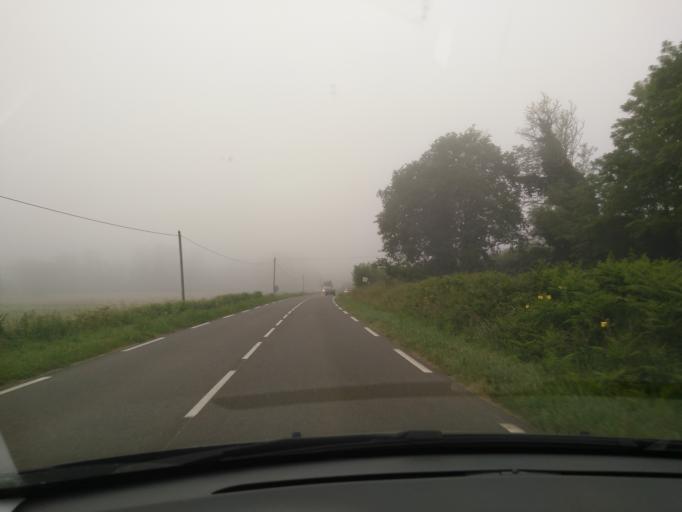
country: FR
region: Aquitaine
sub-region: Departement des Landes
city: Villeneuve-de-Marsan
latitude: 43.8859
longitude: -0.3783
